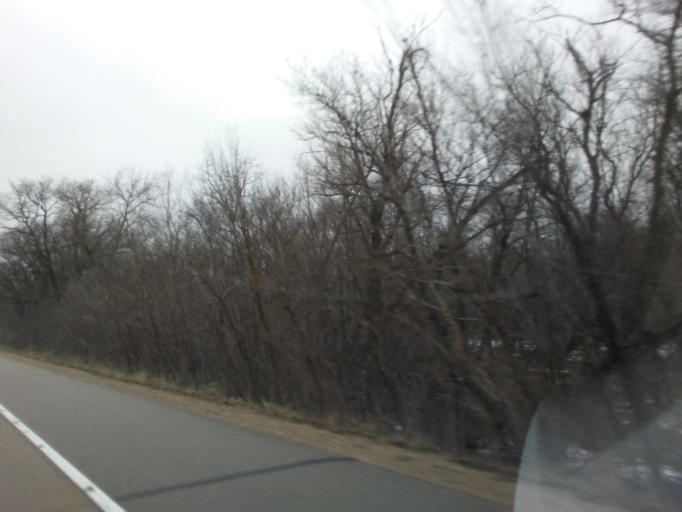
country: US
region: Wisconsin
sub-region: Dane County
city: Mazomanie
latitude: 43.1616
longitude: -89.8546
